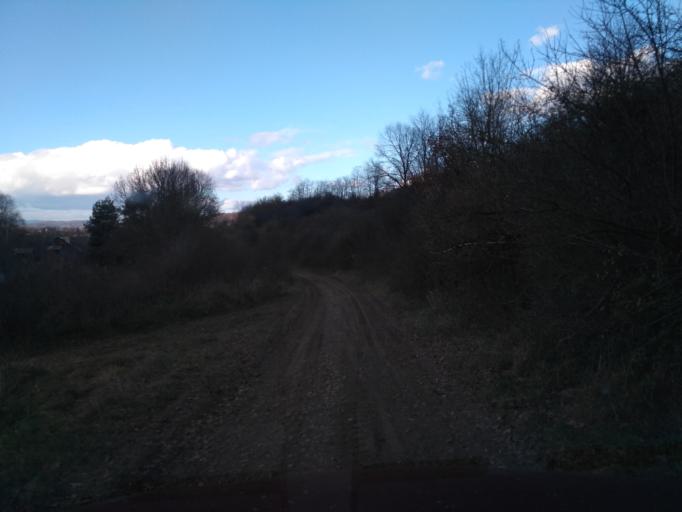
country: SK
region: Presovsky
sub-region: Okres Presov
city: Presov
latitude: 48.9263
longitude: 21.1963
